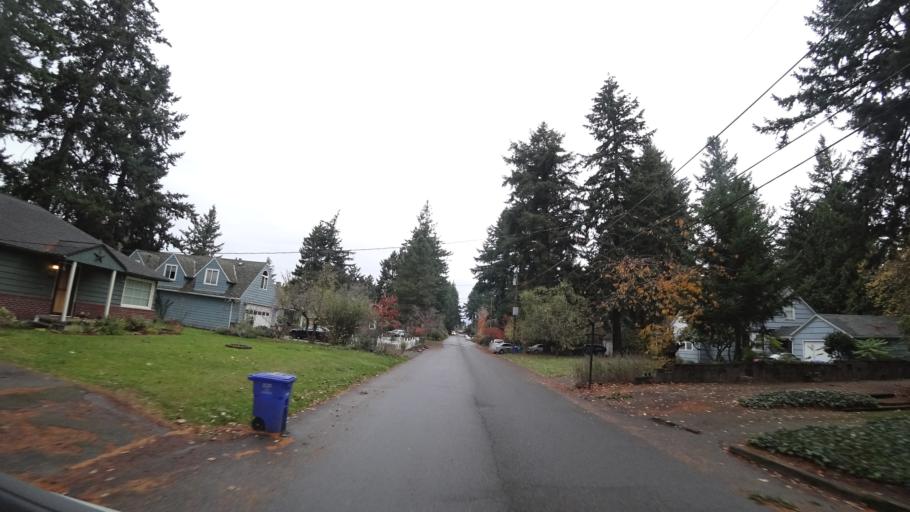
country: US
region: Oregon
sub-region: Multnomah County
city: Lents
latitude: 45.5285
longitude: -122.5484
